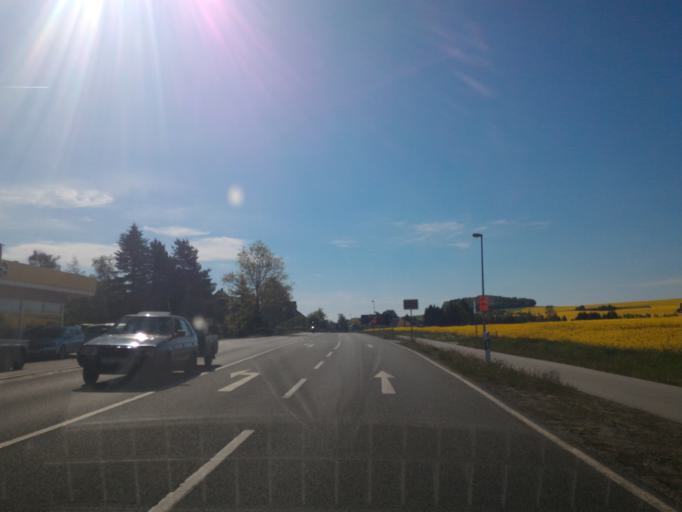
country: DE
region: Saxony
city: Neugersdorf
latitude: 51.0002
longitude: 14.6245
